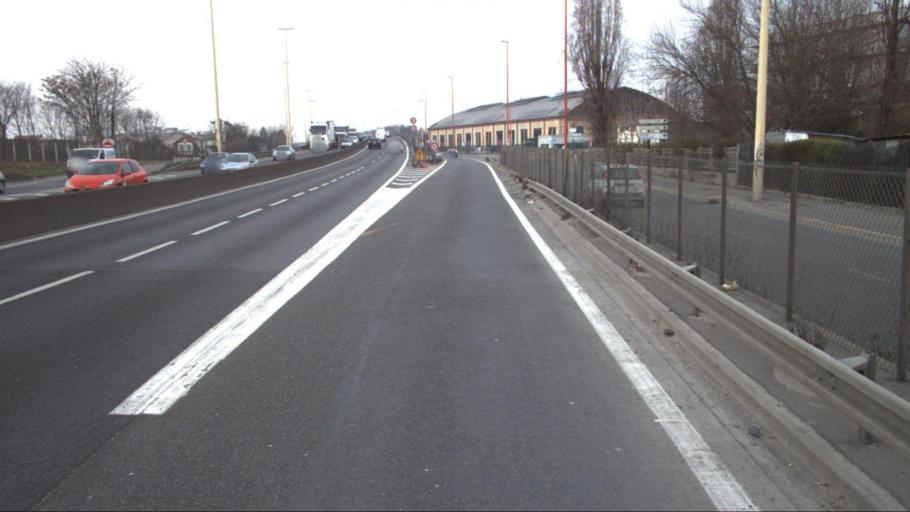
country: FR
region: Ile-de-France
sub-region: Departement des Hauts-de-Seine
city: Colombes
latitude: 48.9324
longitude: 2.2482
